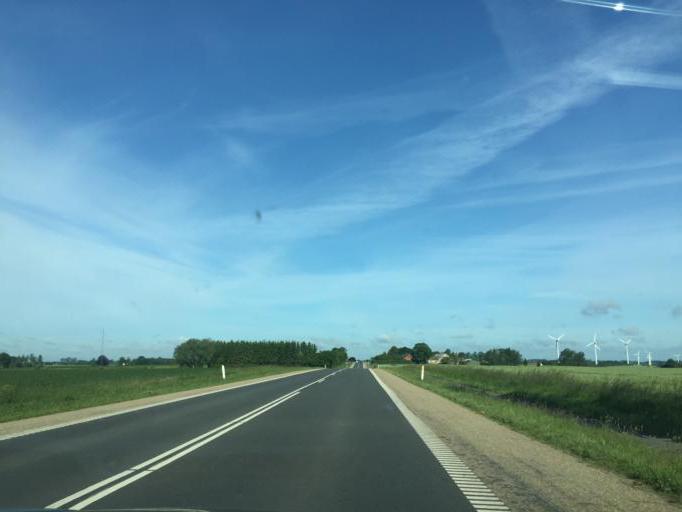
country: DK
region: South Denmark
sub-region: Middelfart Kommune
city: Norre Aby
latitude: 55.4801
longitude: 9.8465
